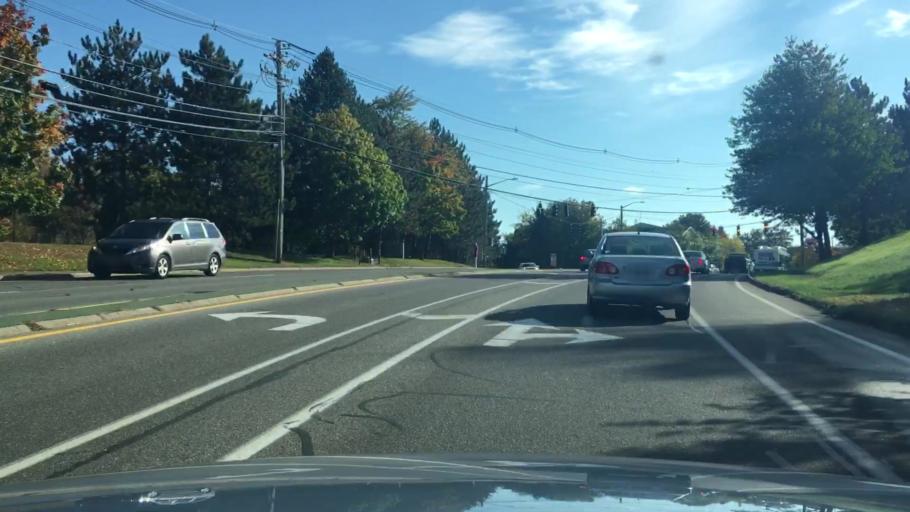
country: US
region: Maine
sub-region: Cumberland County
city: South Portland Gardens
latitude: 43.6599
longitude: -70.3076
